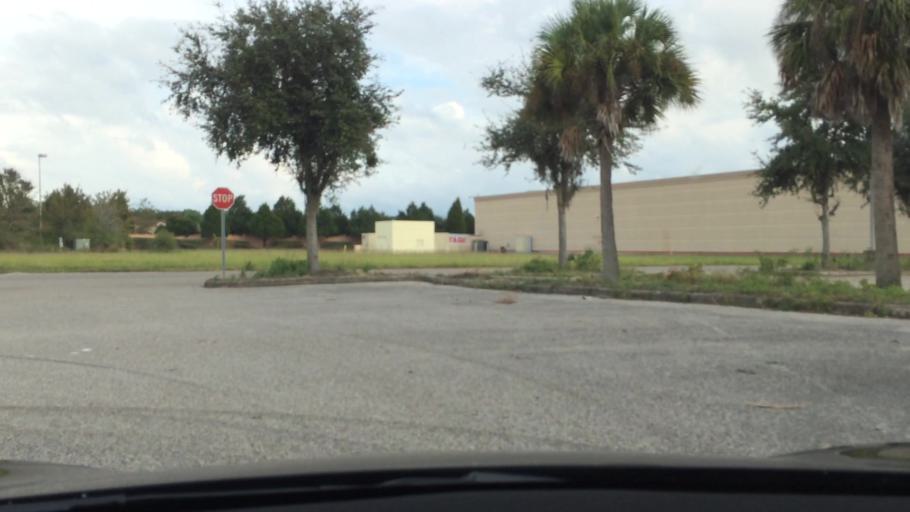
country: US
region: Florida
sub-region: Hillsborough County
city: Lutz
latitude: 28.1746
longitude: -82.4706
